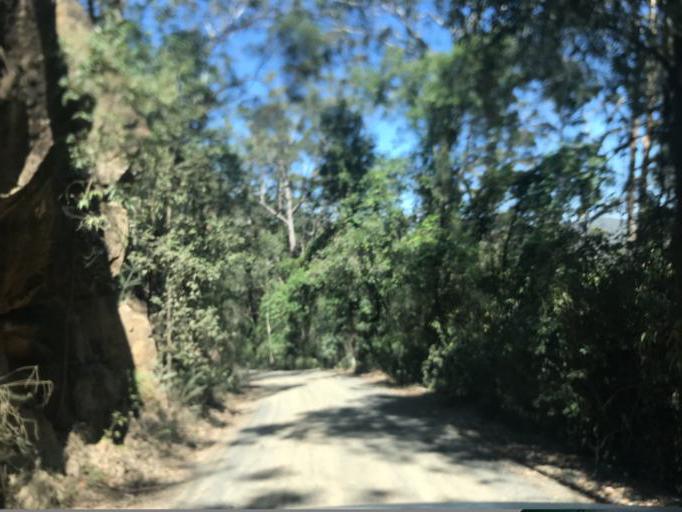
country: AU
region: New South Wales
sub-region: Wyong Shire
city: Little Jilliby
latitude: -33.1530
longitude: 151.0804
